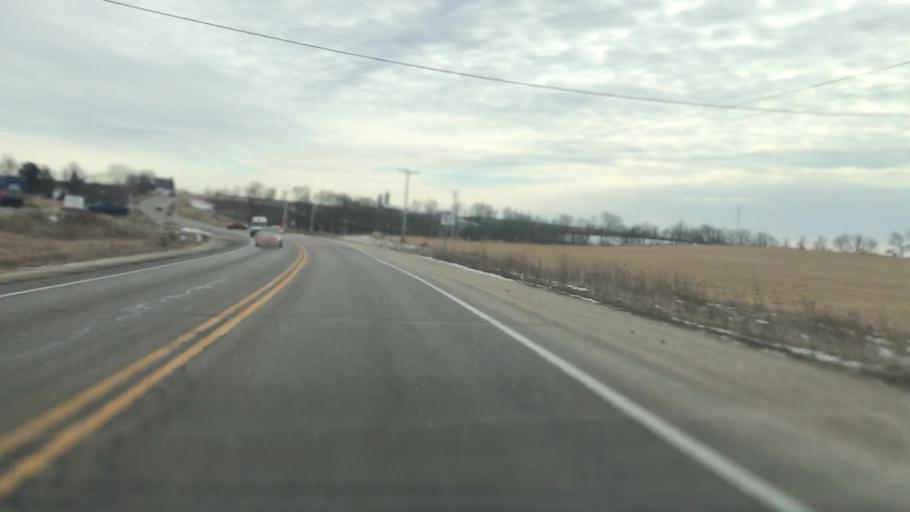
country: US
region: Wisconsin
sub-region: Dodge County
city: Theresa
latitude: 43.4313
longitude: -88.4526
